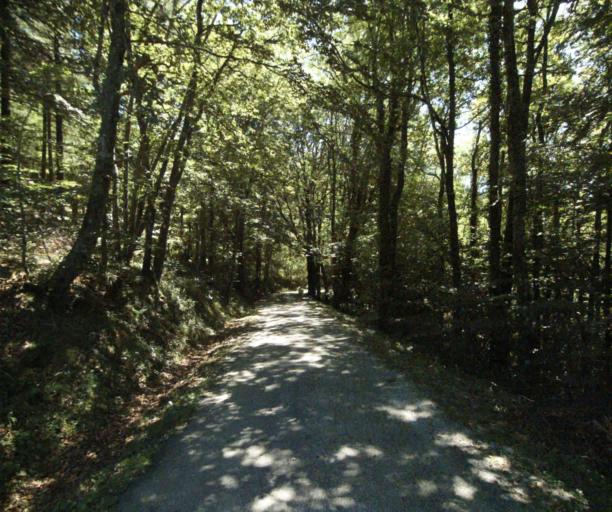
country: FR
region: Midi-Pyrenees
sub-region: Departement du Tarn
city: Dourgne
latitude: 43.4468
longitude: 2.2049
